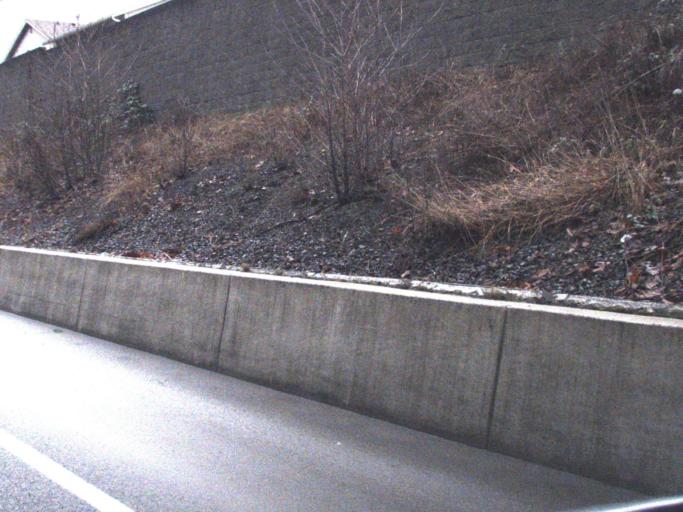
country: US
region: Washington
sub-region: Snohomish County
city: Granite Falls
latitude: 48.0912
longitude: -121.9698
